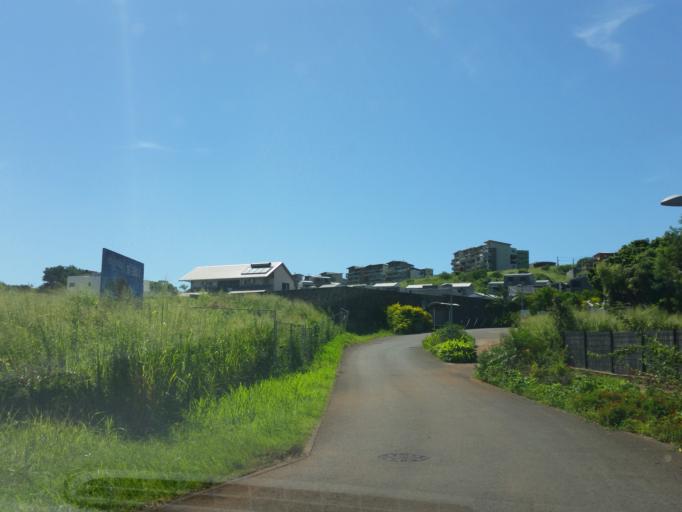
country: RE
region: Reunion
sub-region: Reunion
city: Sainte-Marie
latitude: -20.9177
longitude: 55.5214
